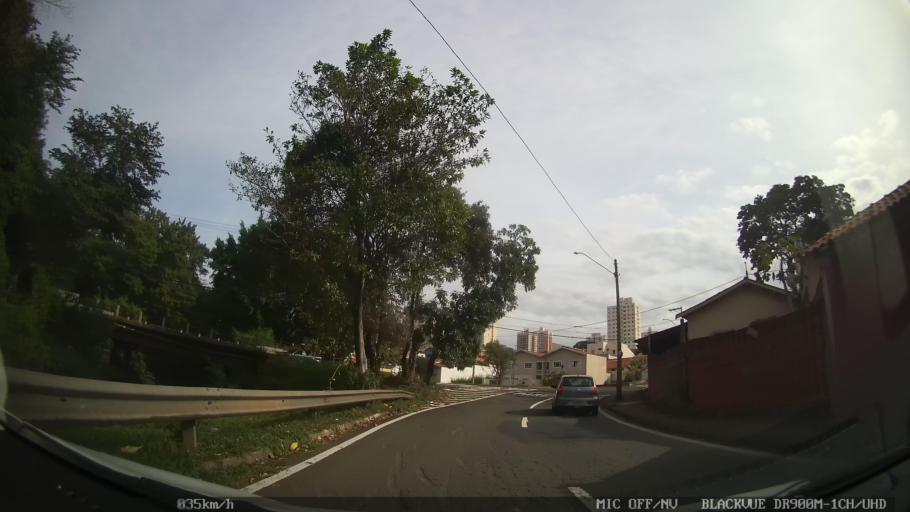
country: BR
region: Sao Paulo
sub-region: Piracicaba
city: Piracicaba
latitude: -22.7195
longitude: -47.6248
